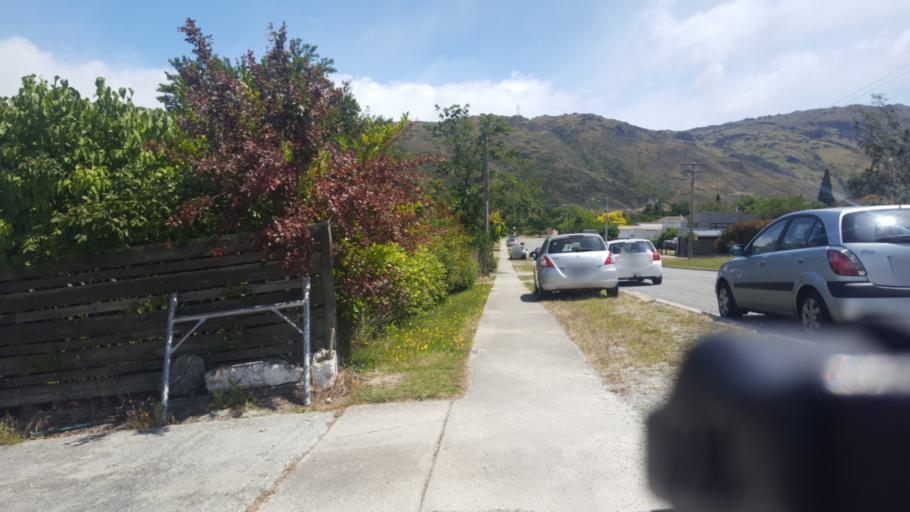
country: NZ
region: Otago
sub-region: Queenstown-Lakes District
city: Wanaka
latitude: -45.1912
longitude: 169.3239
